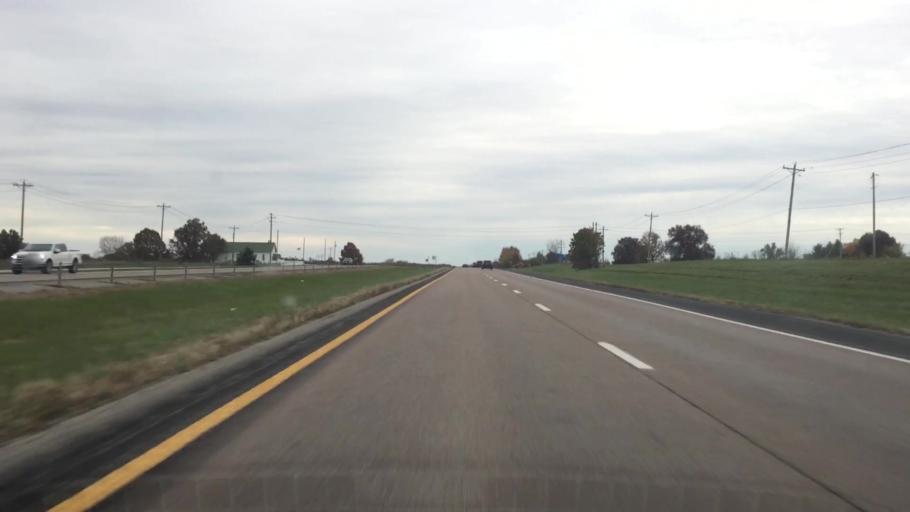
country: US
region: Missouri
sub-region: Boone County
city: Ashland
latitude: 38.7962
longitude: -92.2515
